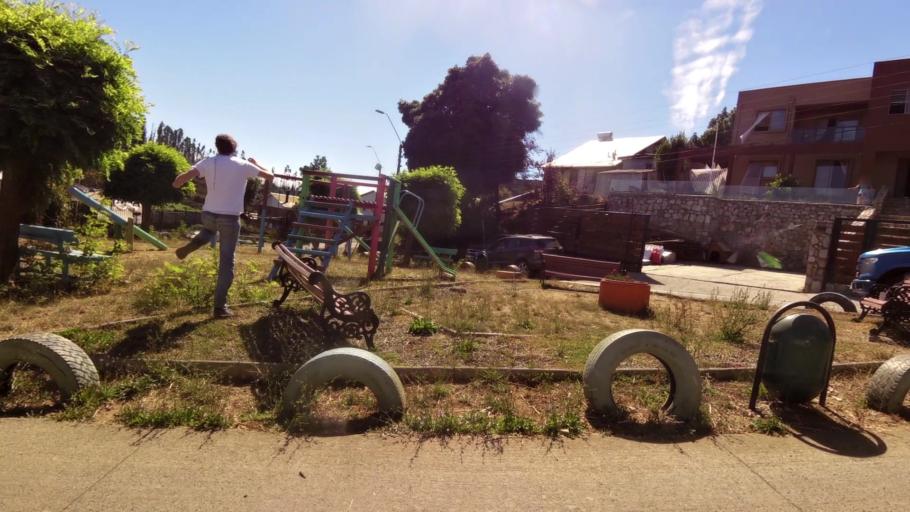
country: CL
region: Biobio
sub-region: Provincia de Concepcion
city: Penco
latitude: -36.7497
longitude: -72.9974
